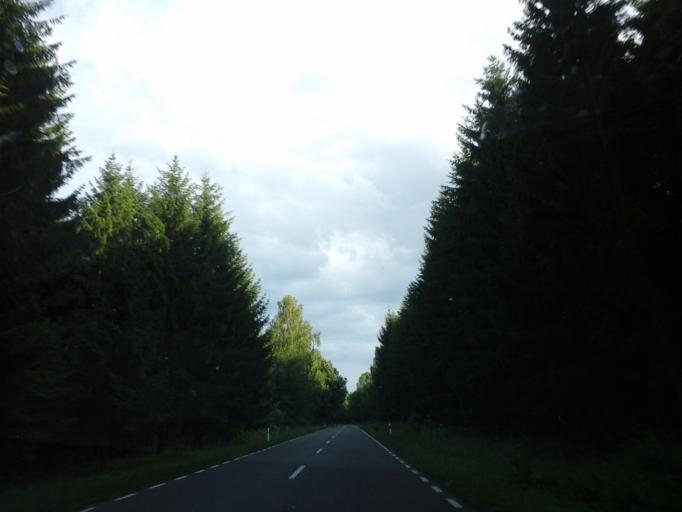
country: PL
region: West Pomeranian Voivodeship
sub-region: Powiat kamienski
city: Golczewo
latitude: 53.8798
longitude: 14.8907
